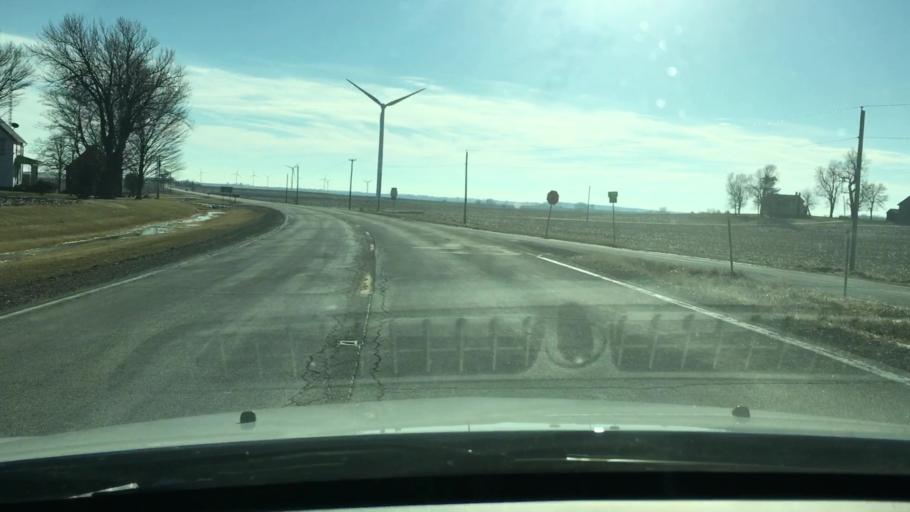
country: US
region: Illinois
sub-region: LaSalle County
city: Mendota
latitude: 41.6817
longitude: -89.1296
